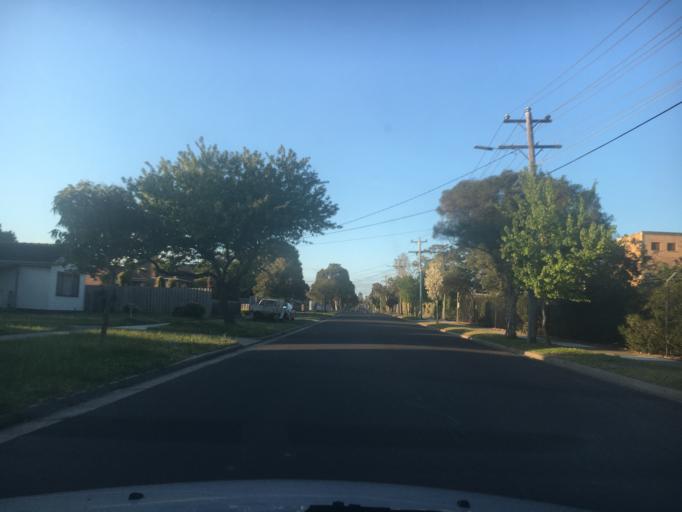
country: AU
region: Victoria
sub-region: Kingston
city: Clayton South
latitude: -37.9278
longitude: 145.1261
